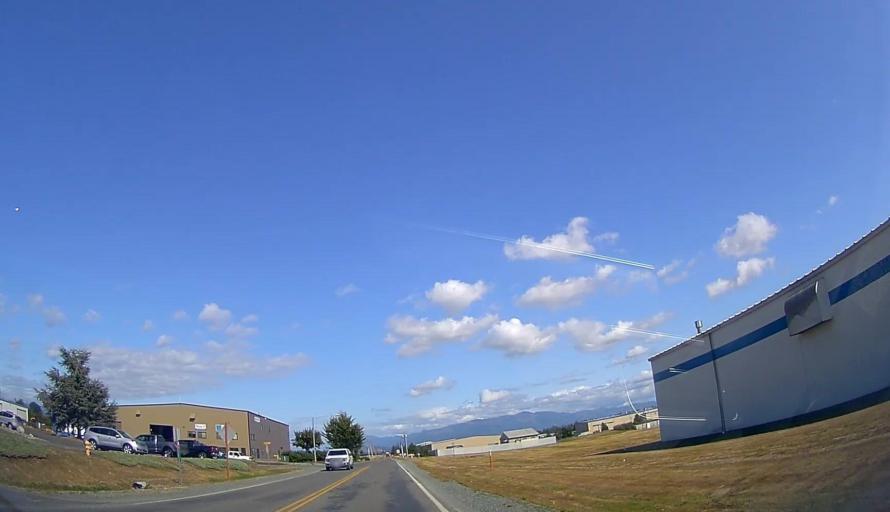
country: US
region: Washington
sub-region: Skagit County
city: Burlington
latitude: 48.4721
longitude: -122.4095
